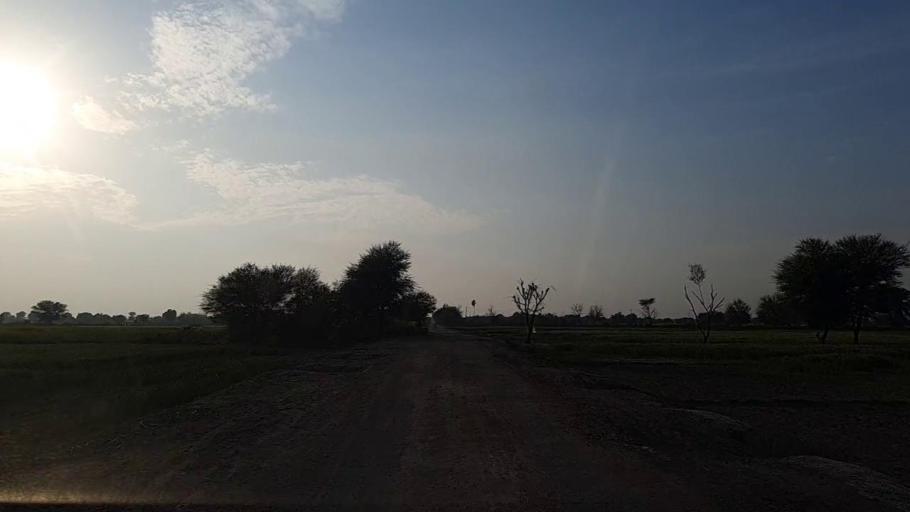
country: PK
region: Sindh
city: Jam Sahib
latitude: 26.3953
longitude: 68.5374
